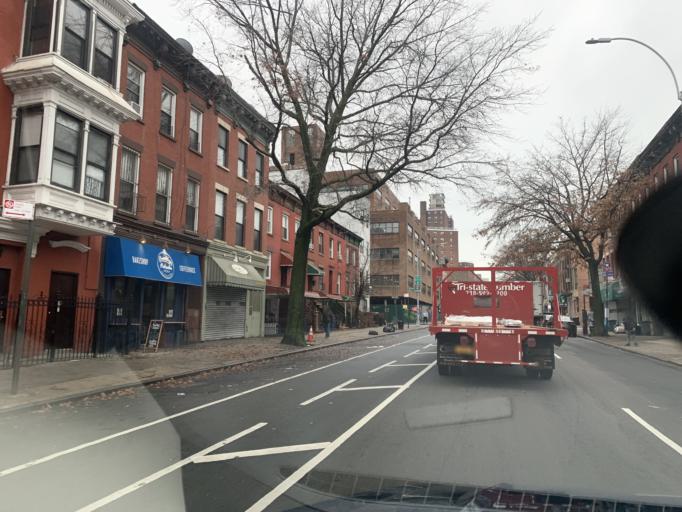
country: US
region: New York
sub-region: Kings County
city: Brooklyn
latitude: 40.6910
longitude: -73.9555
